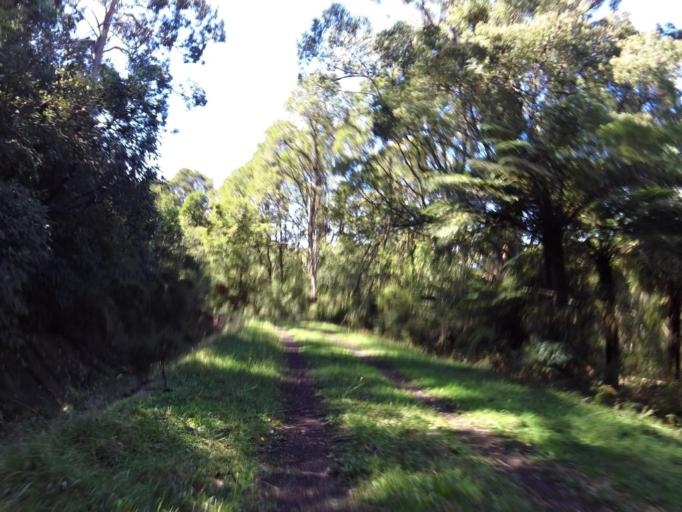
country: AU
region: Victoria
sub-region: Yarra Ranges
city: Millgrove
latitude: -37.7410
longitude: 145.6342
